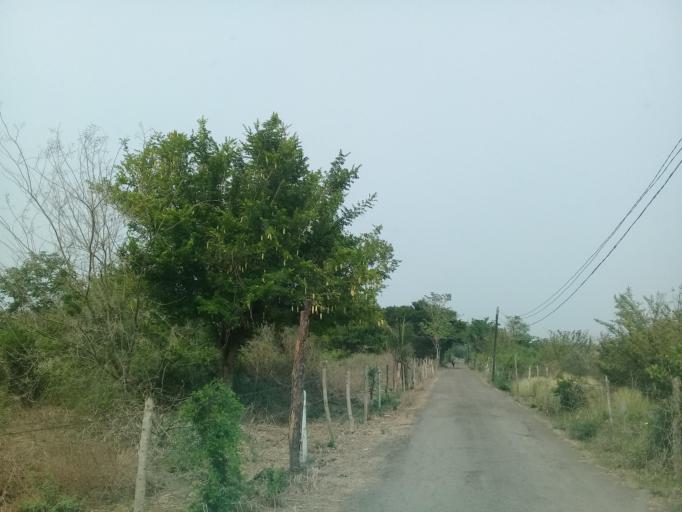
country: MX
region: Veracruz
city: Paso del Toro
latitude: 18.9819
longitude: -96.1773
